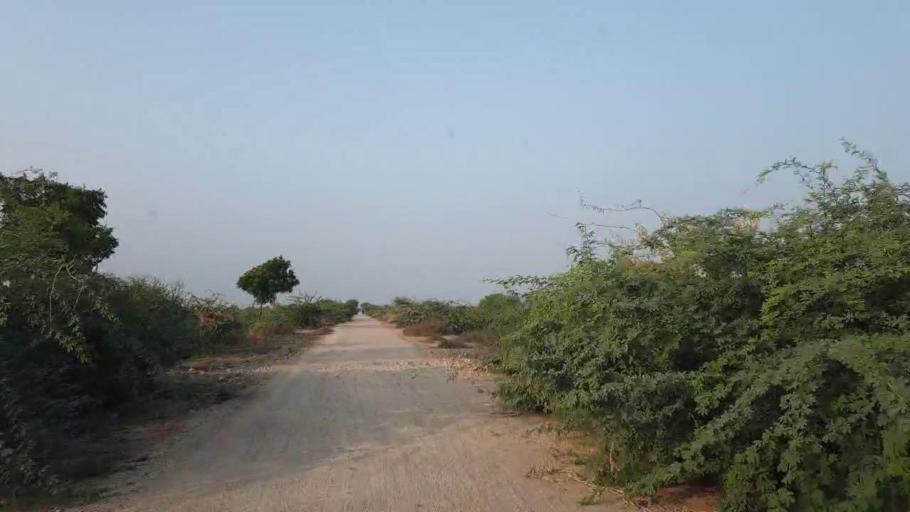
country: PK
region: Sindh
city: Rajo Khanani
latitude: 25.0266
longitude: 68.9772
